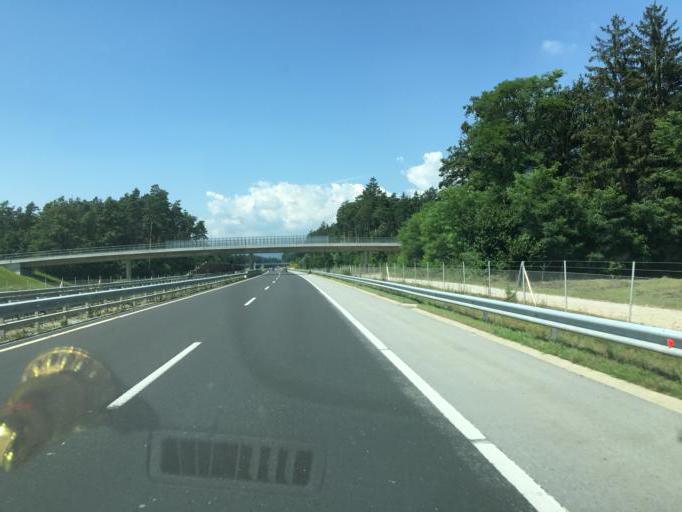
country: SI
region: Starse
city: Starse
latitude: 46.4581
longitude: 15.7334
